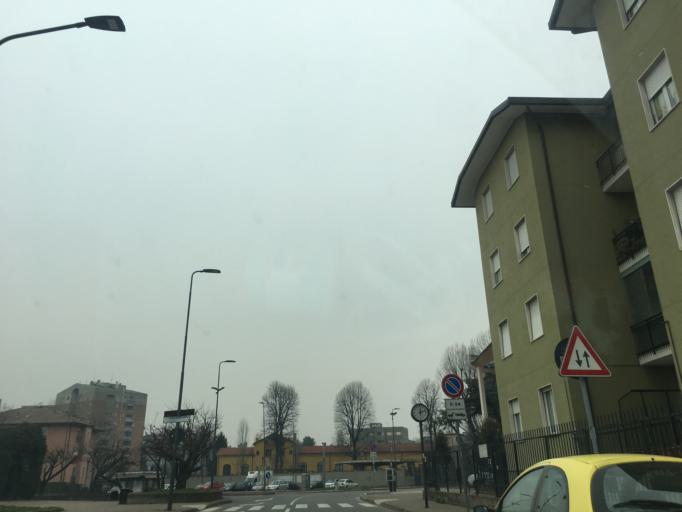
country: IT
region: Lombardy
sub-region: Citta metropolitana di Milano
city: Figino
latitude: 45.4764
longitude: 9.0896
